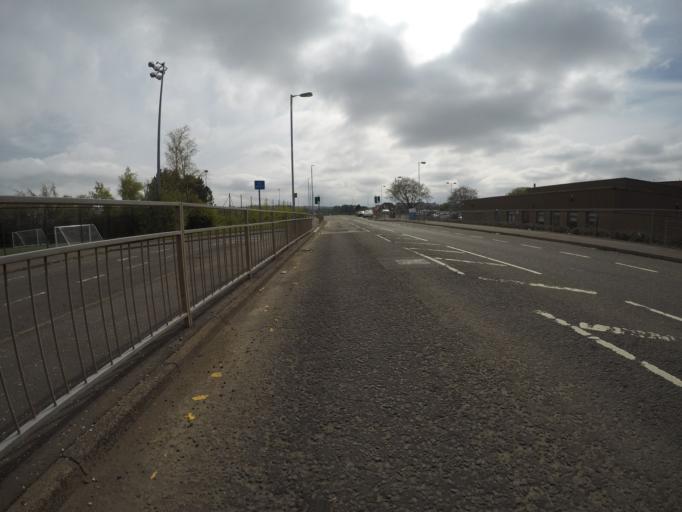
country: GB
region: Scotland
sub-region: East Renfrewshire
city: Newton Mearns
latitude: 55.7690
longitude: -4.3064
